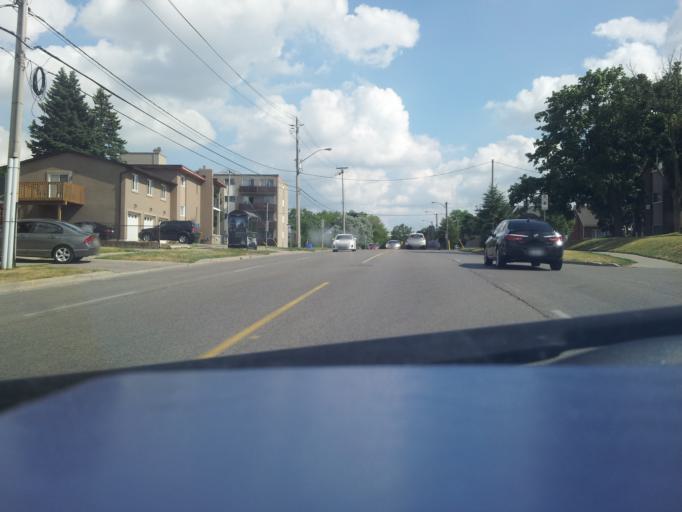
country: CA
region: Ontario
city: Kitchener
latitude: 43.4454
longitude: -80.5131
